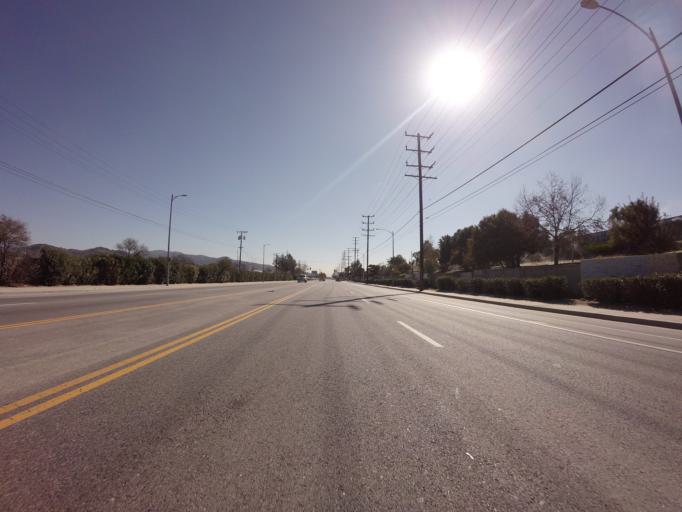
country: US
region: California
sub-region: Los Angeles County
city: North Hollywood
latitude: 34.2415
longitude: -118.3788
